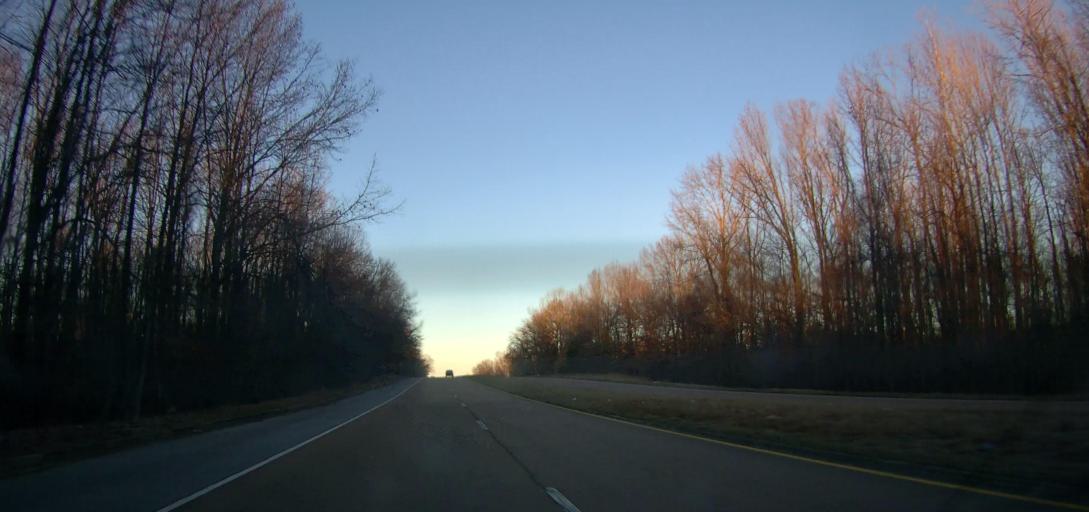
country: US
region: Tennessee
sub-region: Shelby County
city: Bartlett
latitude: 35.2477
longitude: -89.8963
